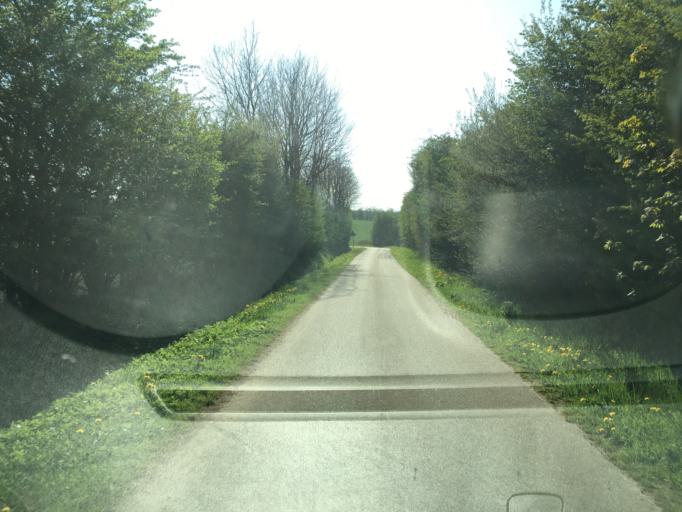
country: DK
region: South Denmark
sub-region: Tonder Kommune
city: Toftlund
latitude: 55.1672
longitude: 9.0989
